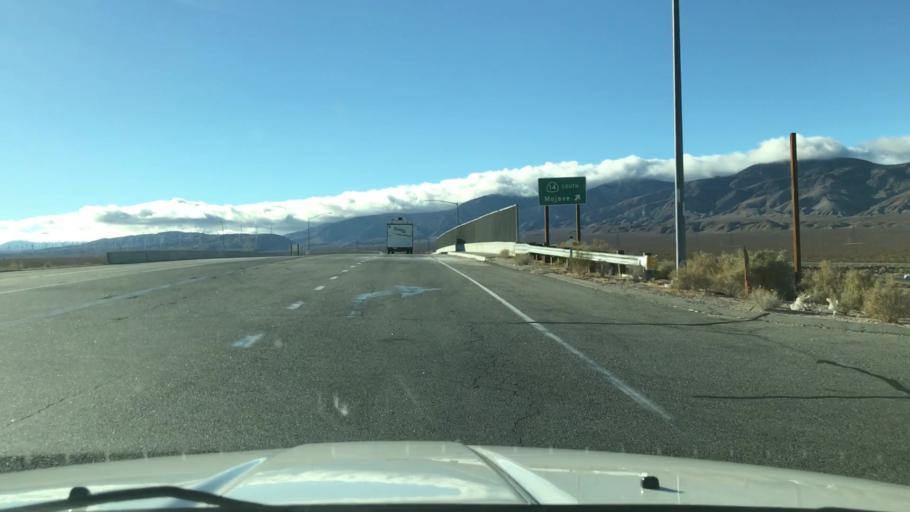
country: US
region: California
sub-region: Kern County
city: Mojave
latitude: 35.1255
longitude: -118.1229
